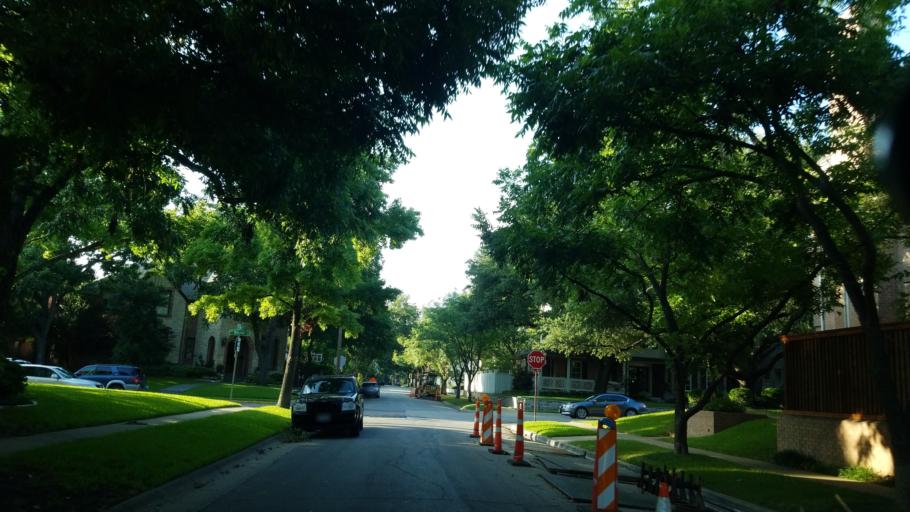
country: US
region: Texas
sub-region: Dallas County
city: University Park
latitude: 32.8458
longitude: -96.7928
